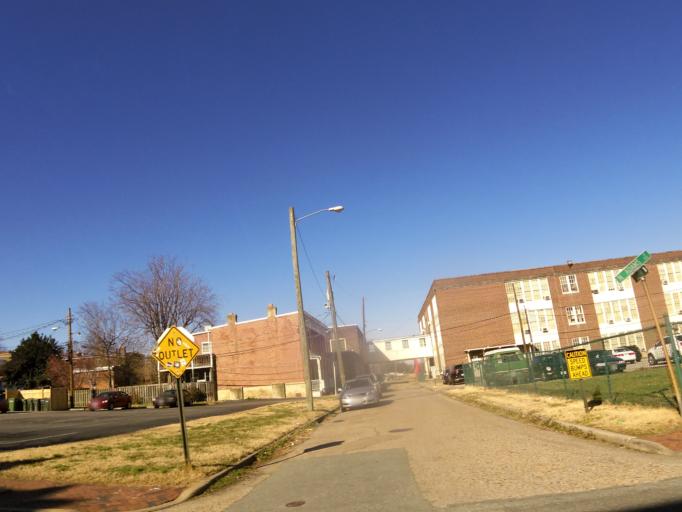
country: US
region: Virginia
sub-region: City of Richmond
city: Richmond
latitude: 37.5485
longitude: -77.4407
